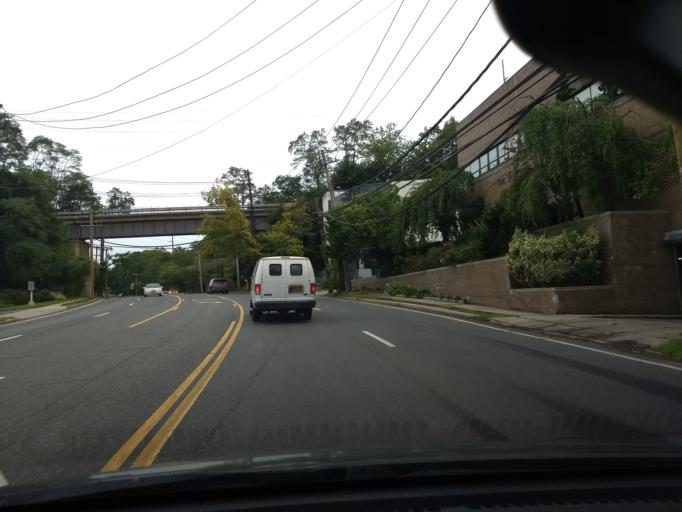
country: US
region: New York
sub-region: Nassau County
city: Thomaston
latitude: 40.7928
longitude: -73.7120
